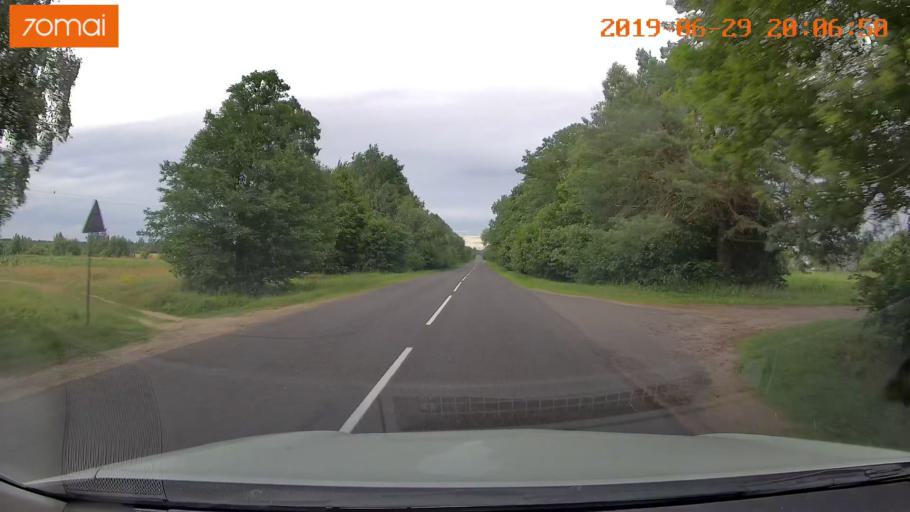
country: BY
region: Brest
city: Lahishyn
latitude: 52.3397
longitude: 26.0216
